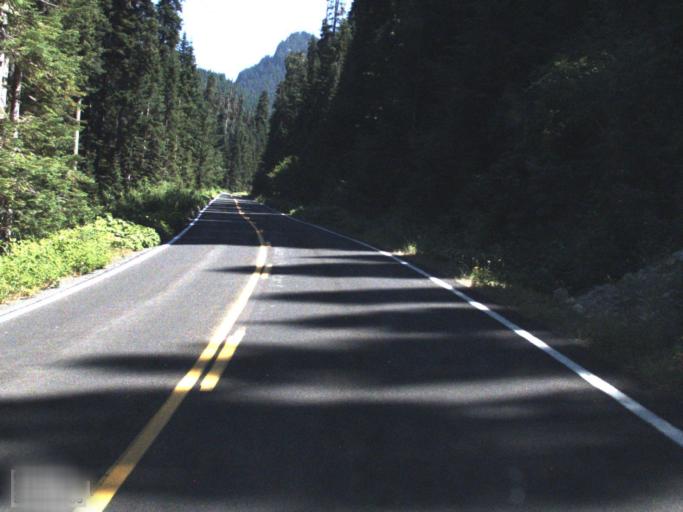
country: US
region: Washington
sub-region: King County
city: Enumclaw
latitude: 46.8324
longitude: -121.5269
